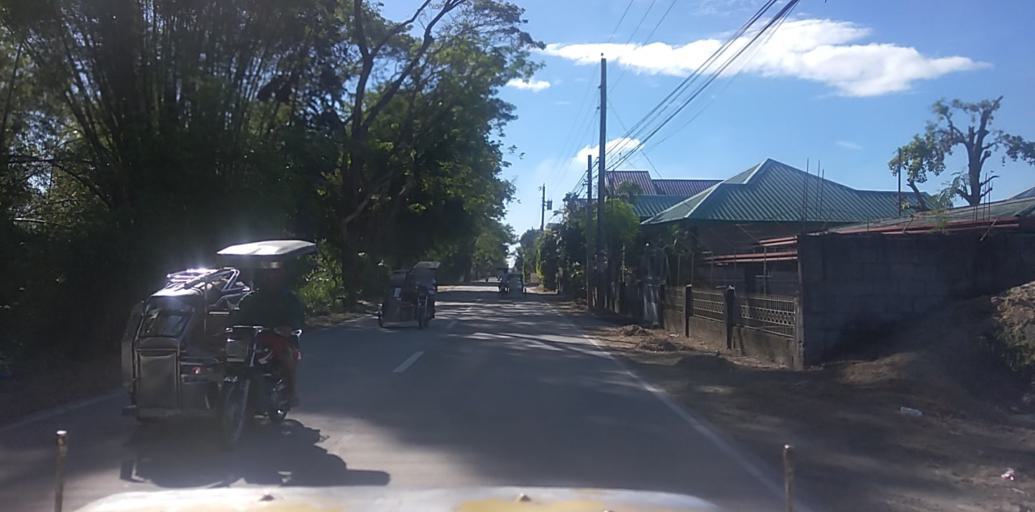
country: PH
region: Central Luzon
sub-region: Province of Pampanga
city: San Patricio
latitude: 15.0885
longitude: 120.7139
